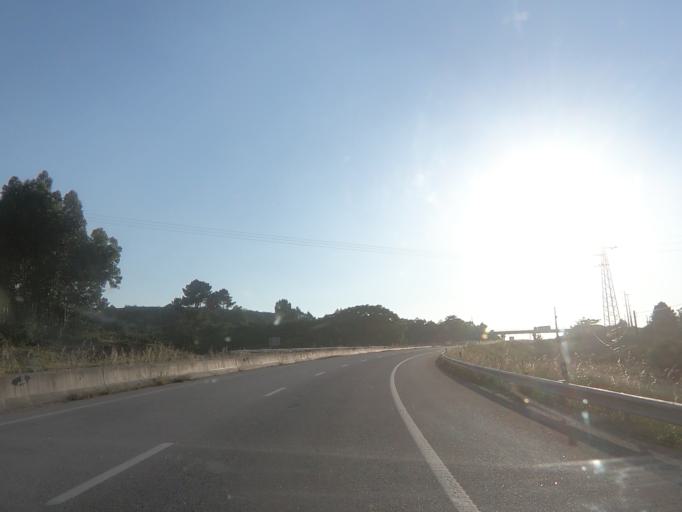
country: PT
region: Guarda
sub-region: Celorico da Beira
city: Celorico da Beira
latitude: 40.6262
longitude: -7.3662
